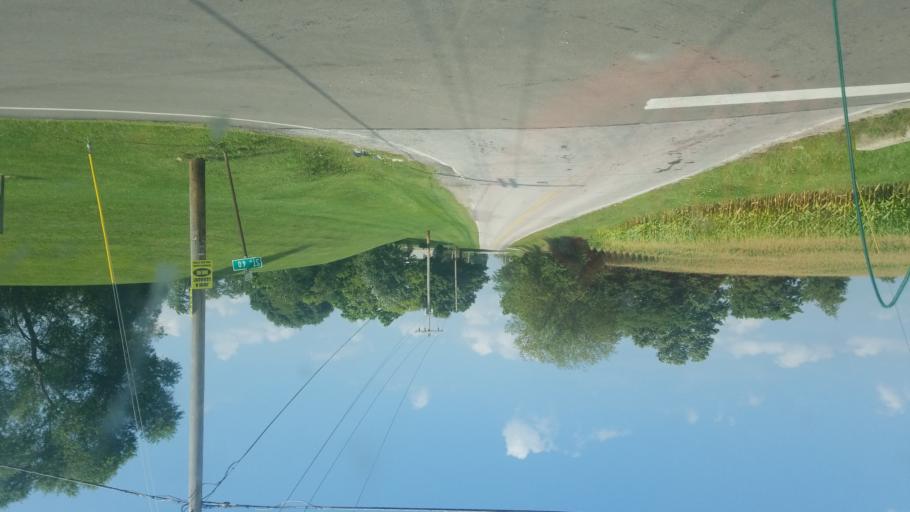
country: US
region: Ohio
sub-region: Huron County
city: New London
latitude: 41.0656
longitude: -82.3967
